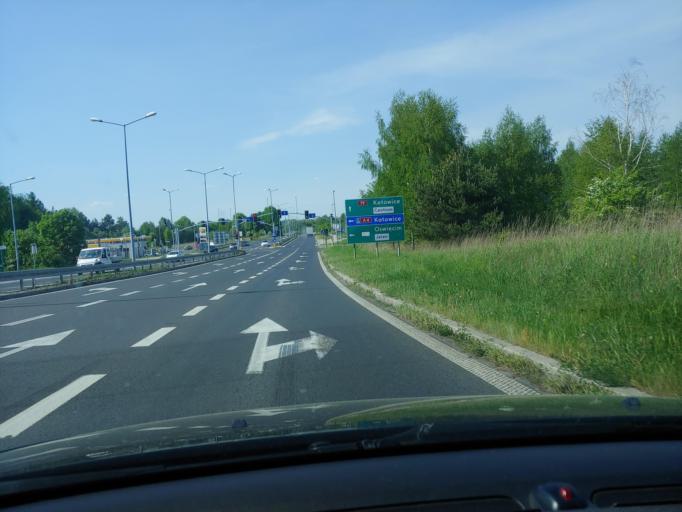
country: PL
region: Silesian Voivodeship
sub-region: Jaworzno
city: Jaworzno
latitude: 50.1736
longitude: 19.2949
